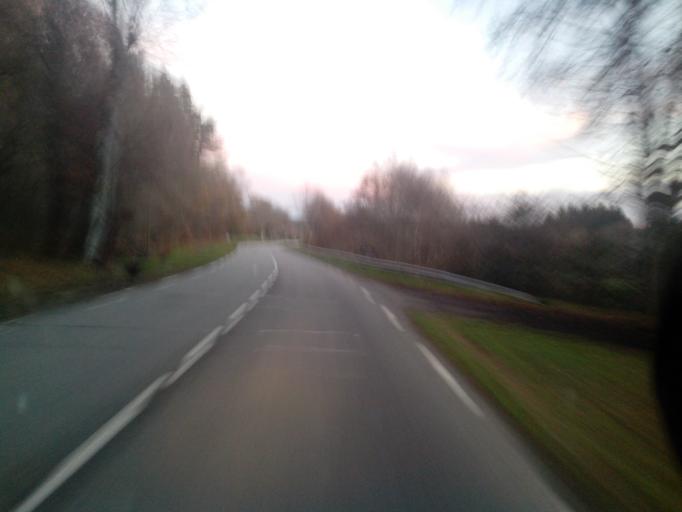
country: FR
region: Limousin
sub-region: Departement de la Correze
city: Meymac
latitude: 45.5120
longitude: 2.1878
